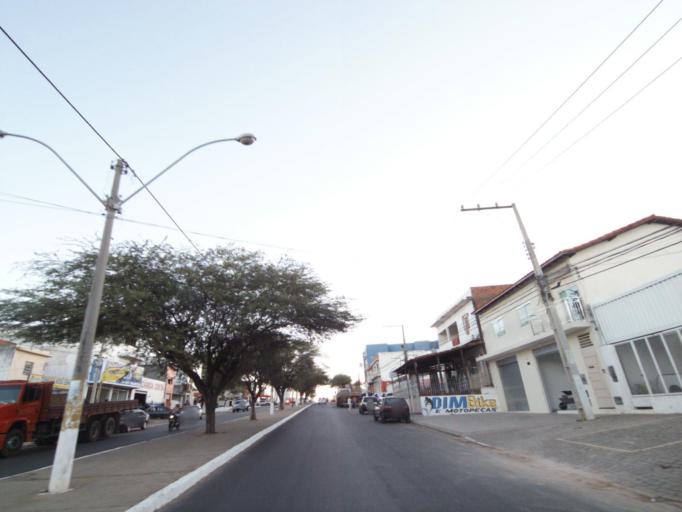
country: BR
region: Bahia
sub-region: Brumado
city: Brumado
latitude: -14.2137
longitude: -41.6772
